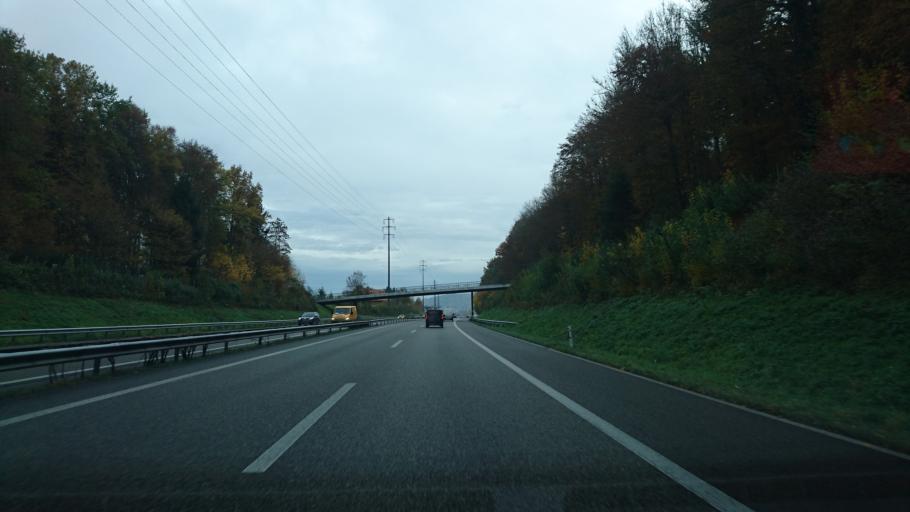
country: CH
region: Aargau
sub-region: Bezirk Zofingen
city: Kolliken
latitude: 47.3266
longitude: 8.0259
